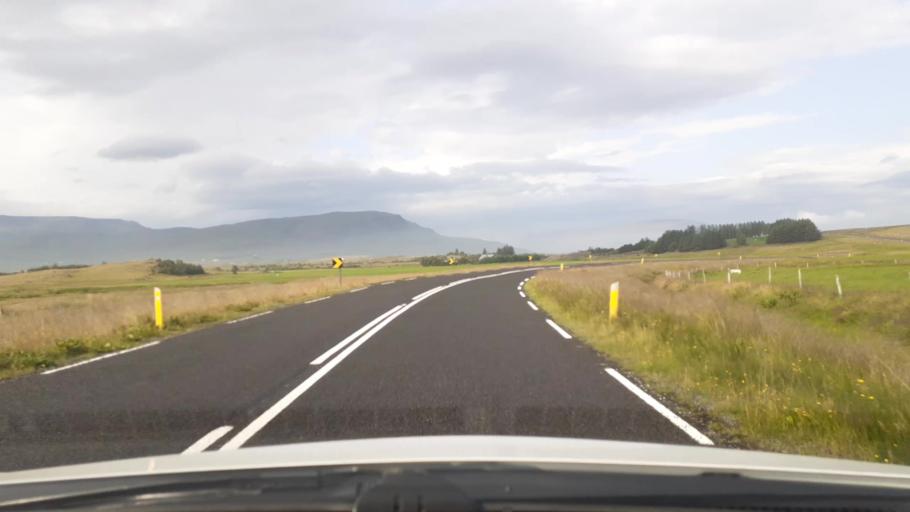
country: IS
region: Capital Region
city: Mosfellsbaer
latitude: 64.3412
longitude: -21.5786
